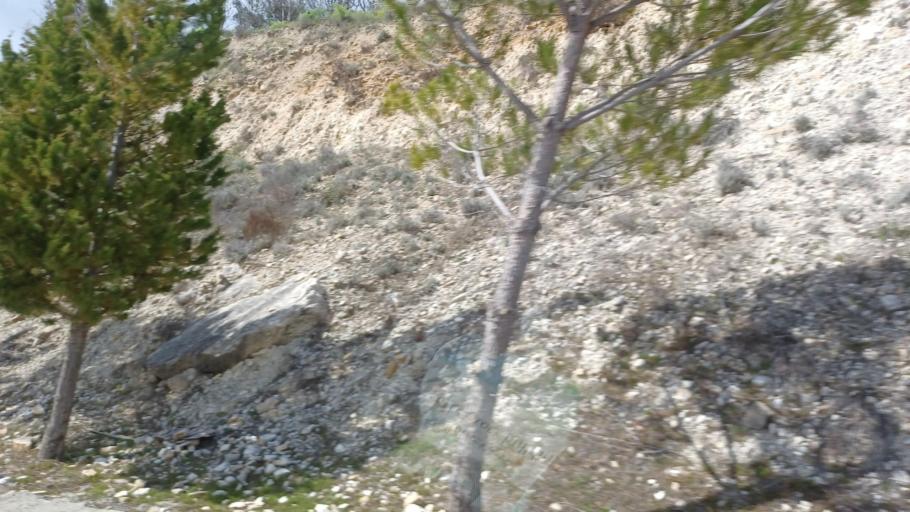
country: CY
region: Limassol
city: Pachna
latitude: 34.8589
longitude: 32.7241
